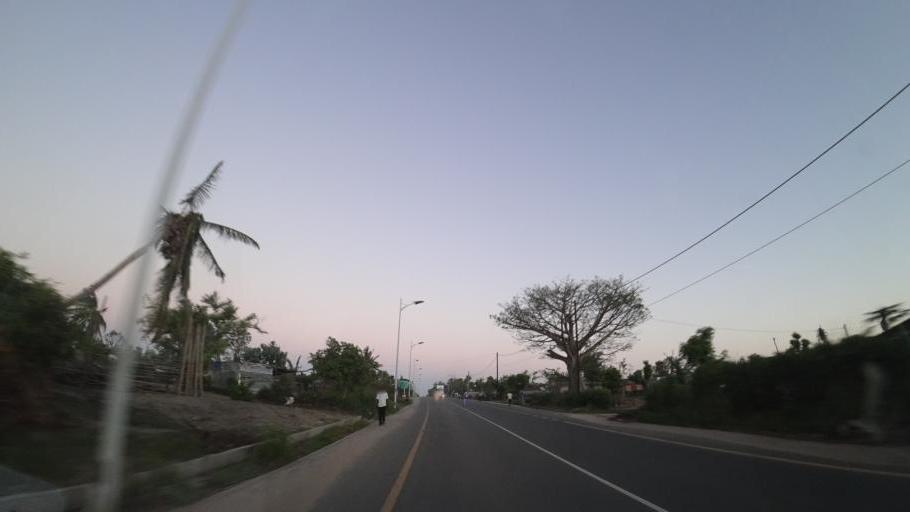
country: MZ
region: Sofala
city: Dondo
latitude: -19.5328
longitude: 34.6299
